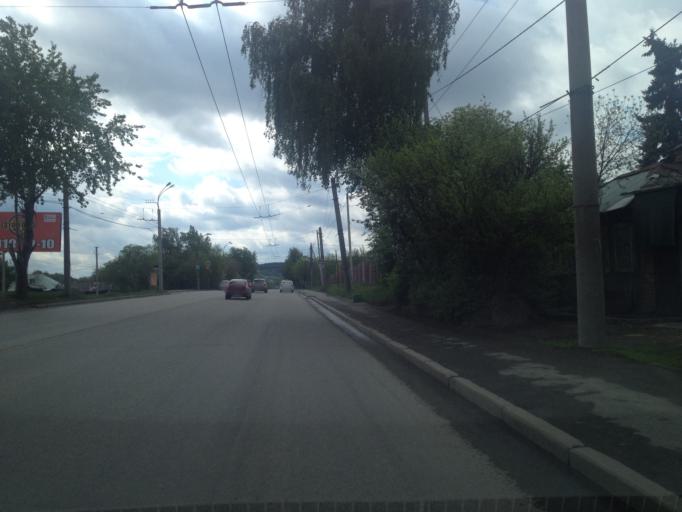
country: RU
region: Sverdlovsk
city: Istok
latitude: 56.7545
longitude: 60.6751
